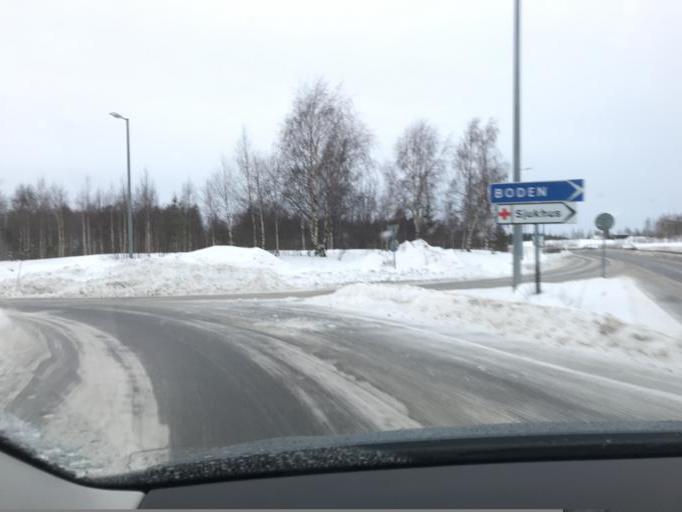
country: SE
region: Norrbotten
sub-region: Lulea Kommun
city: Sodra Sunderbyn
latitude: 65.6686
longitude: 21.9417
